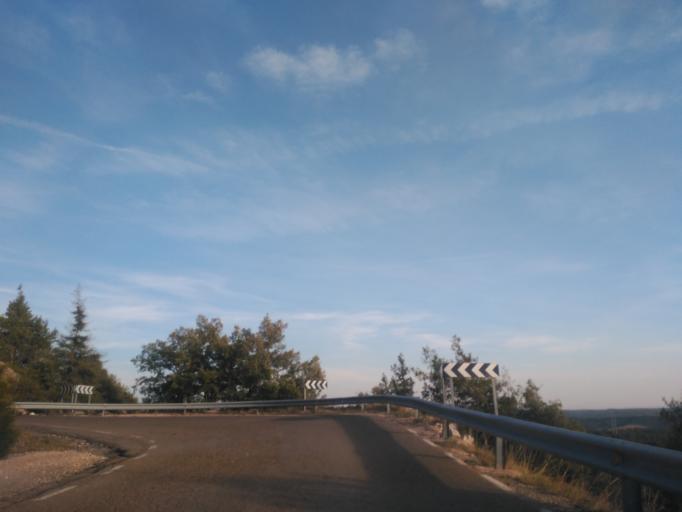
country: ES
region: Castille and Leon
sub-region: Provincia de Soria
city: Ucero
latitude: 41.7287
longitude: -3.0412
